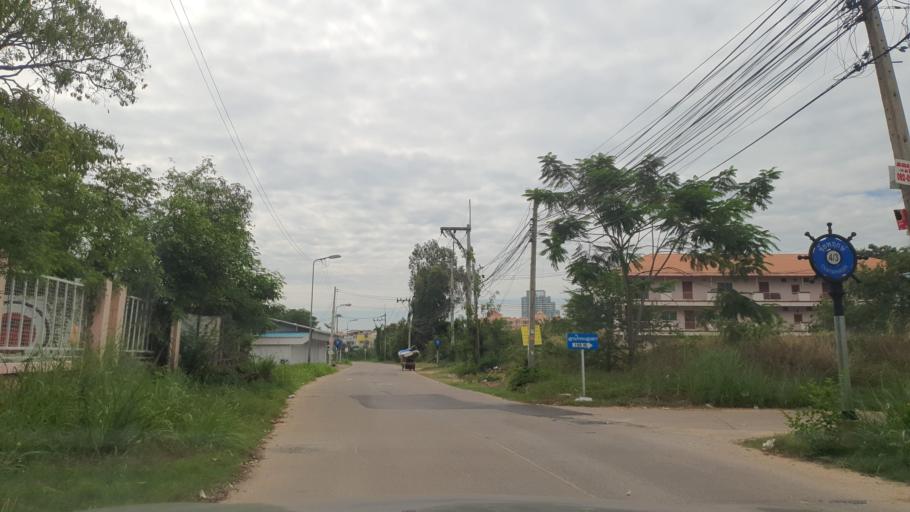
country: TH
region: Chon Buri
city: Phatthaya
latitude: 12.8819
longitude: 100.8895
